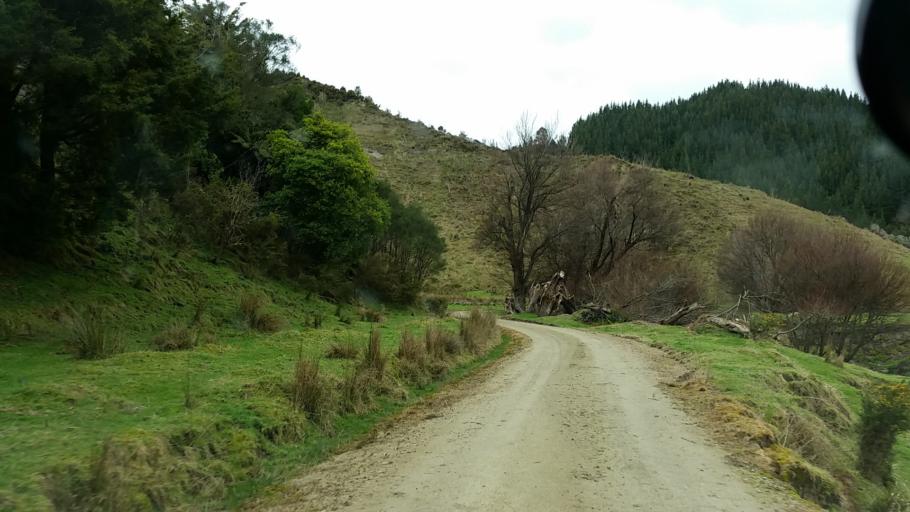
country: NZ
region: Taranaki
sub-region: South Taranaki District
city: Patea
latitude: -39.6569
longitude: 174.7516
